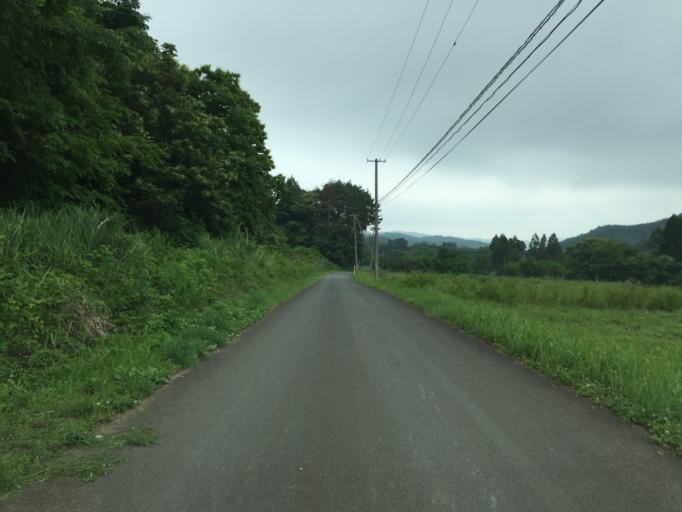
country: JP
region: Fukushima
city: Yanagawamachi-saiwaicho
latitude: 37.7629
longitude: 140.7034
